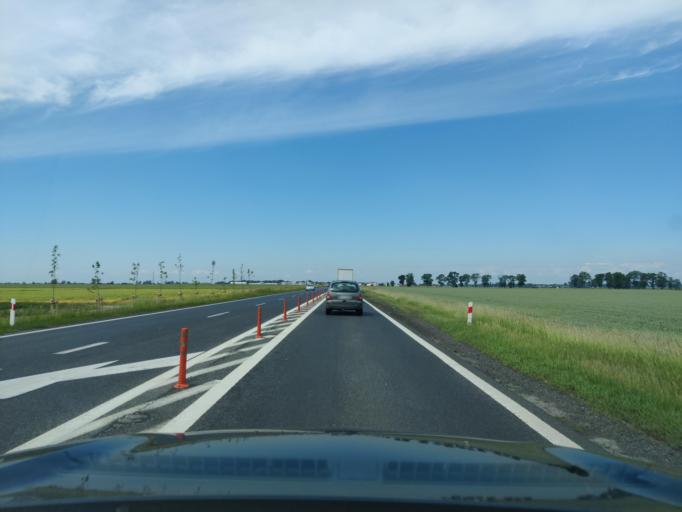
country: PL
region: Greater Poland Voivodeship
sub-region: Powiat grodziski
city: Granowo
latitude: 52.2216
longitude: 16.5642
